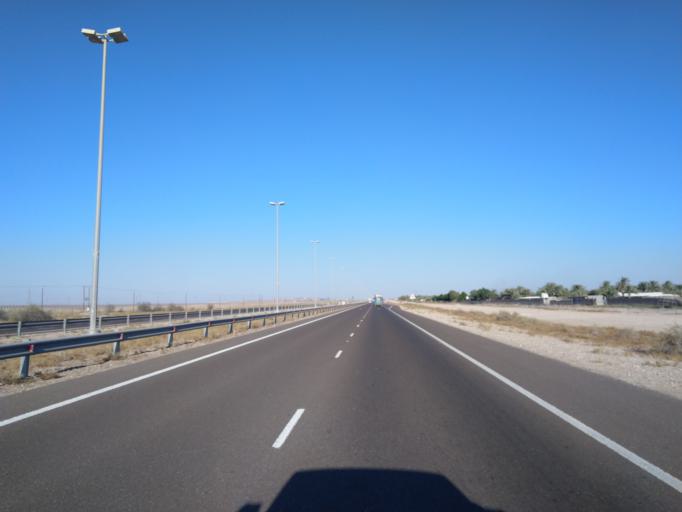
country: OM
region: Al Buraimi
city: Al Buraymi
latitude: 24.4896
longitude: 55.4037
